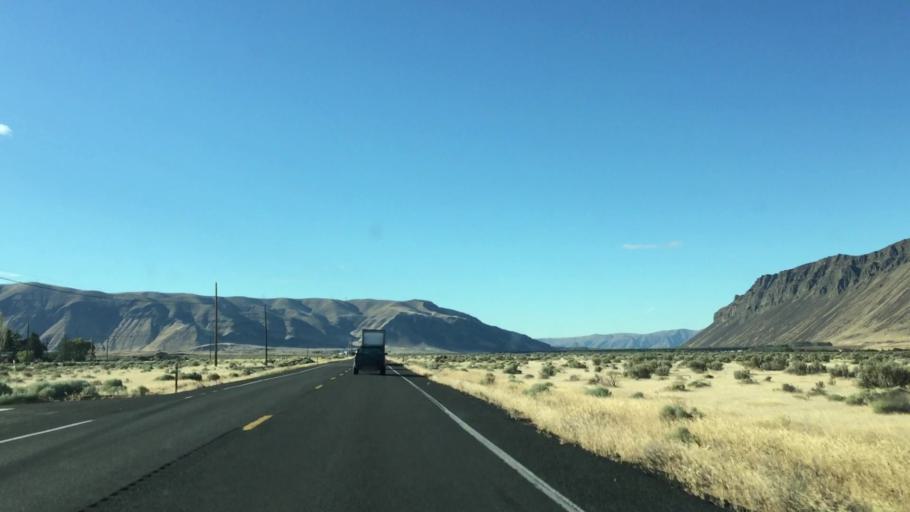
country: US
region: Washington
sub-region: Grant County
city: Mattawa
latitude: 46.8629
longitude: -119.9514
